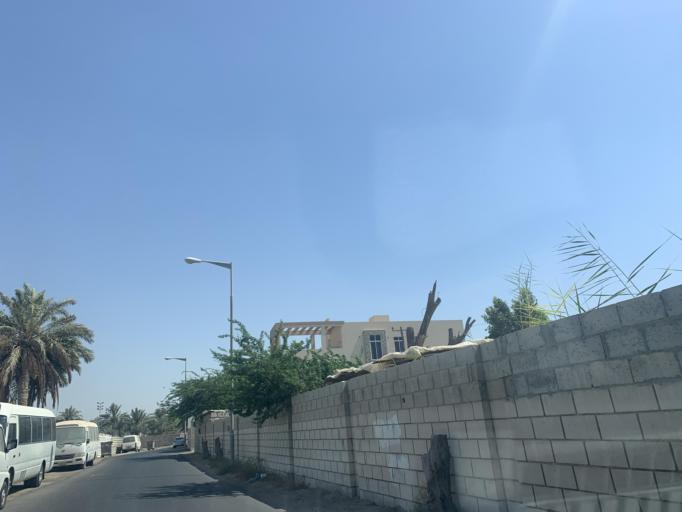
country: BH
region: Manama
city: Jidd Hafs
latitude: 26.2244
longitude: 50.5072
